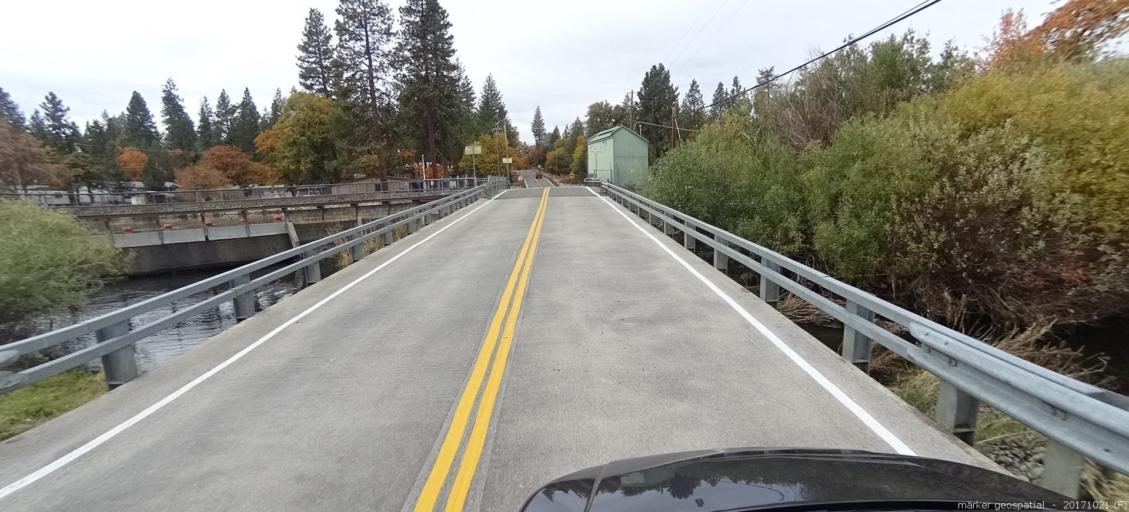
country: US
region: California
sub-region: Shasta County
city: Burney
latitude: 40.9192
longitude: -121.5515
